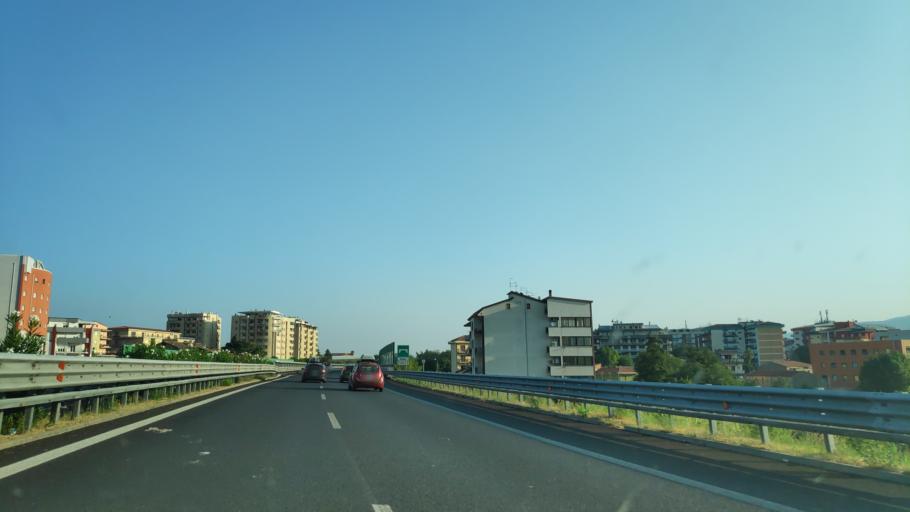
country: IT
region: Calabria
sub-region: Provincia di Cosenza
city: Cosenza
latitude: 39.3212
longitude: 16.2403
